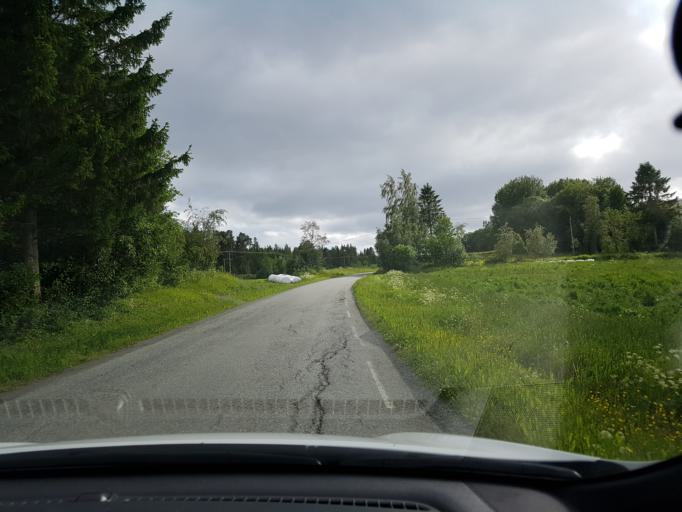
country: NO
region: Nord-Trondelag
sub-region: Frosta
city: Frosta
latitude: 63.6155
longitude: 10.7522
